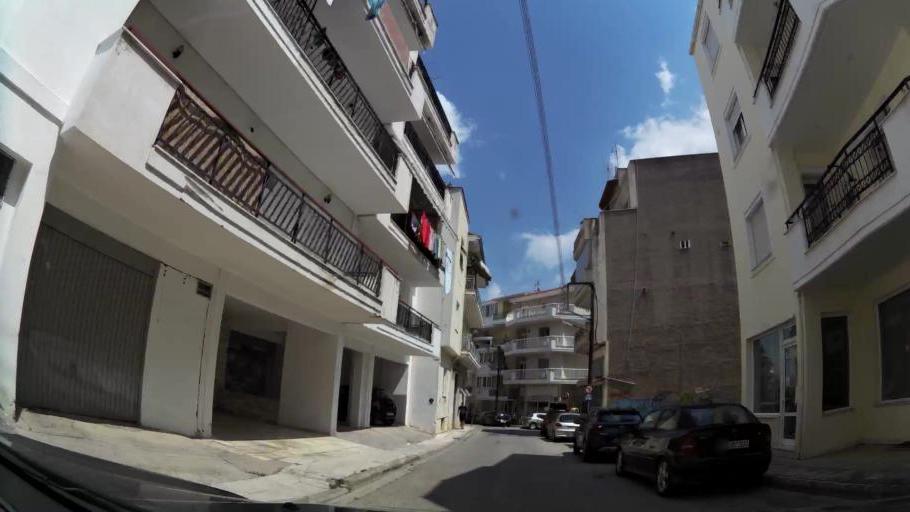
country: GR
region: West Macedonia
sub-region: Nomos Kozanis
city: Kozani
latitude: 40.2973
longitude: 21.7882
